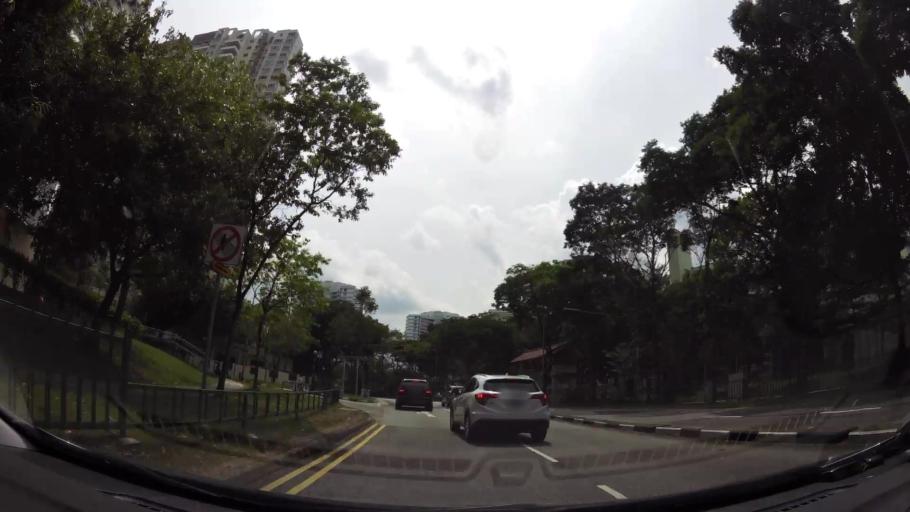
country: MY
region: Johor
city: Johor Bahru
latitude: 1.3497
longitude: 103.7479
